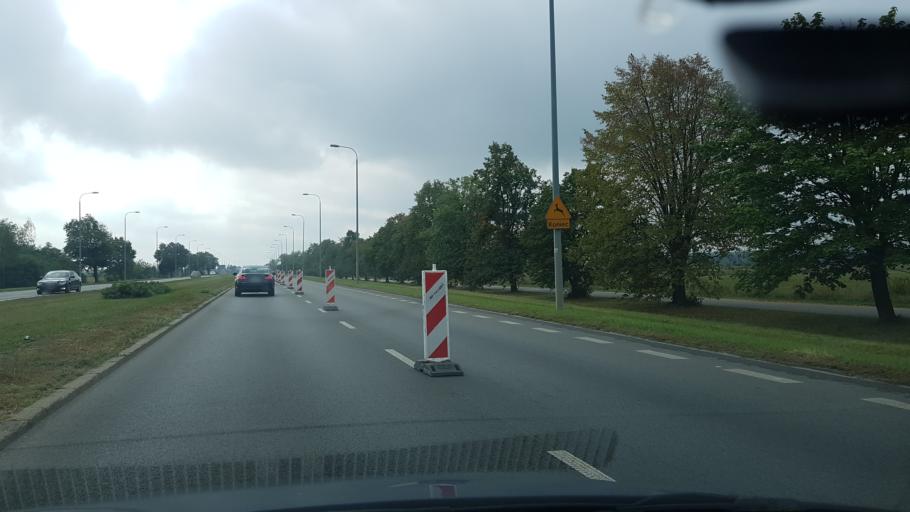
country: PL
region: Masovian Voivodeship
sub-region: Warszawa
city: Kabaty
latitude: 52.1424
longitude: 21.0964
